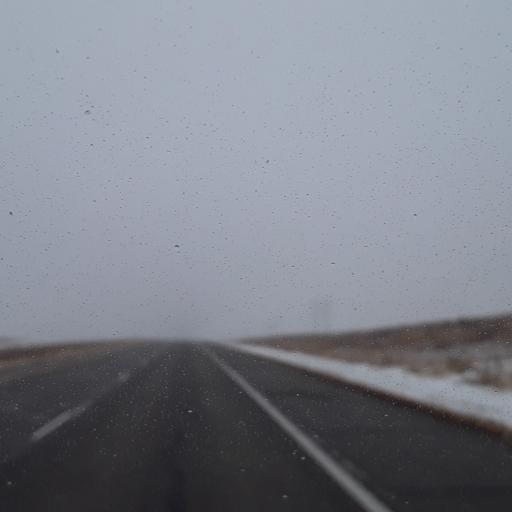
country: US
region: Colorado
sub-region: Logan County
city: Sterling
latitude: 40.7854
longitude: -102.9030
